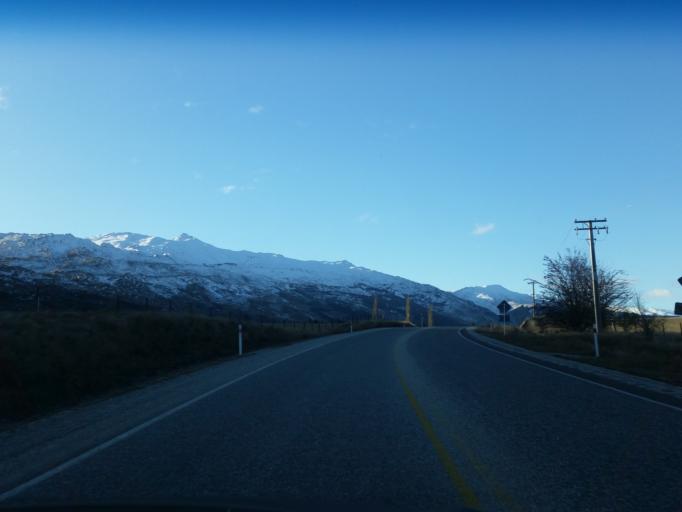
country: NZ
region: Otago
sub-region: Queenstown-Lakes District
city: Queenstown
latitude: -44.9697
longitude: 168.7030
